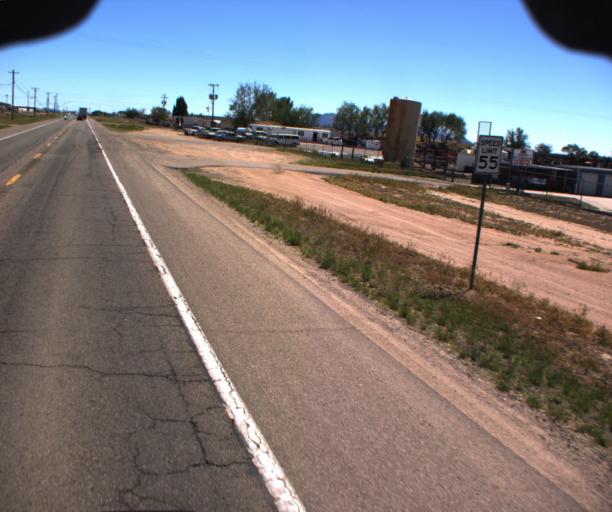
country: US
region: Arizona
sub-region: Yavapai County
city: Chino Valley
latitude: 34.7952
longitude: -112.4512
